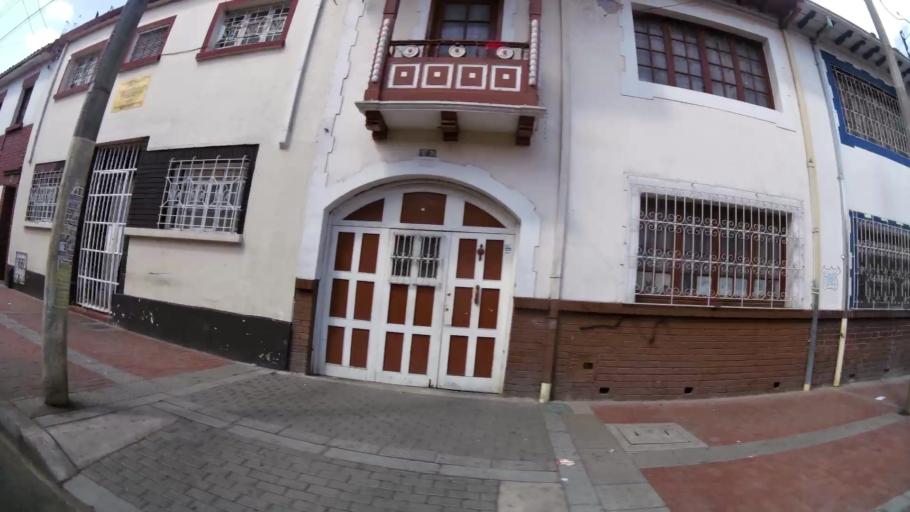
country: CO
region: Bogota D.C.
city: Bogota
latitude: 4.6143
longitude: -74.0770
